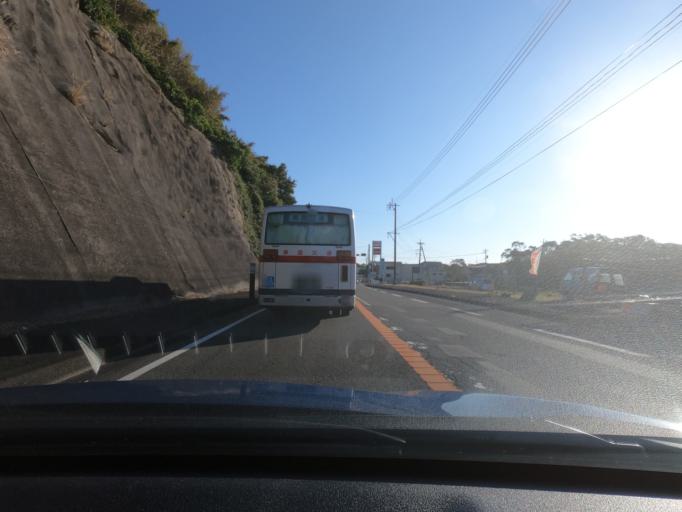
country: JP
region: Kagoshima
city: Akune
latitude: 31.9828
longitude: 130.2037
